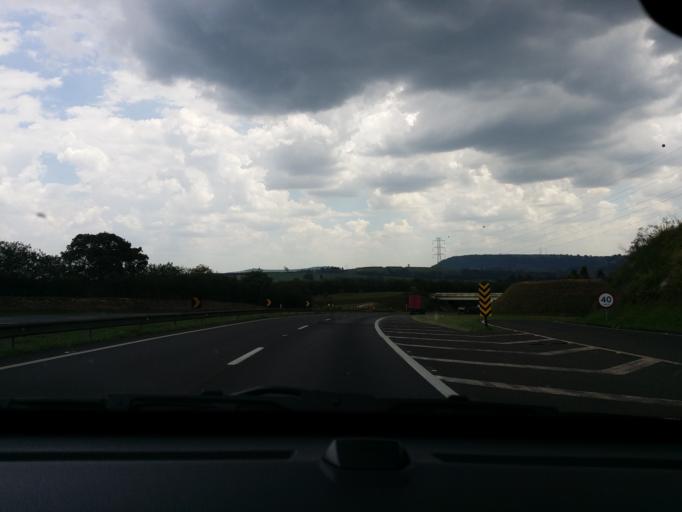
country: BR
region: Sao Paulo
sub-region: Rio Claro
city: Rio Claro
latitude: -22.3127
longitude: -47.6653
